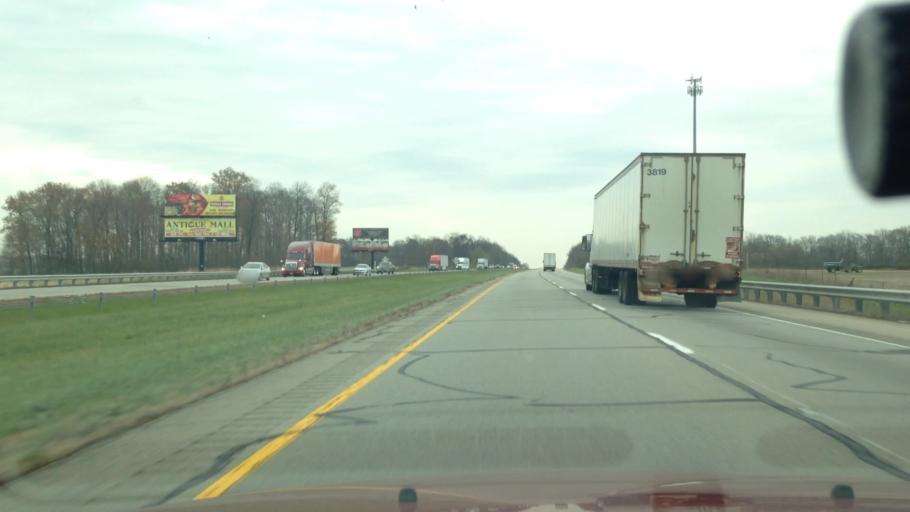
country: US
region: Indiana
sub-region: Wayne County
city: Cambridge City
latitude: 39.8535
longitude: -85.2247
